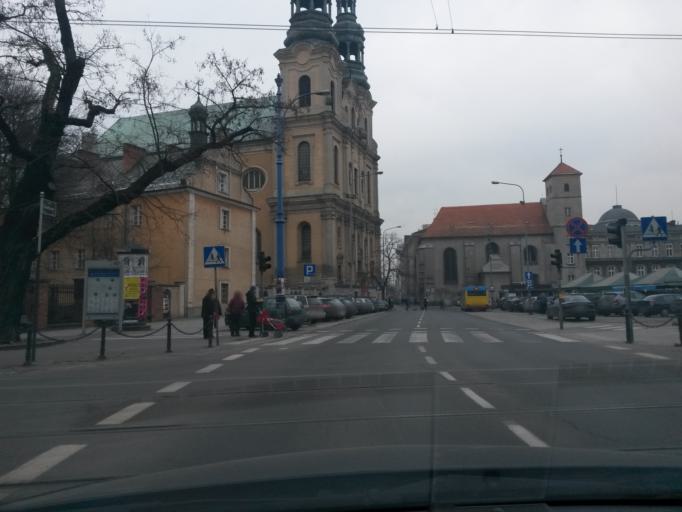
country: PL
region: Greater Poland Voivodeship
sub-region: Poznan
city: Poznan
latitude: 52.4044
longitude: 16.9374
